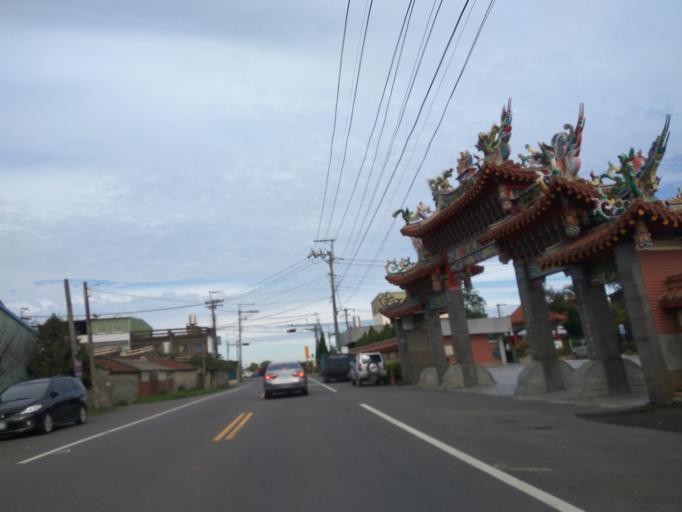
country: TW
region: Taiwan
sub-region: Hsinchu
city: Zhubei
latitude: 24.9597
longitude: 121.1178
